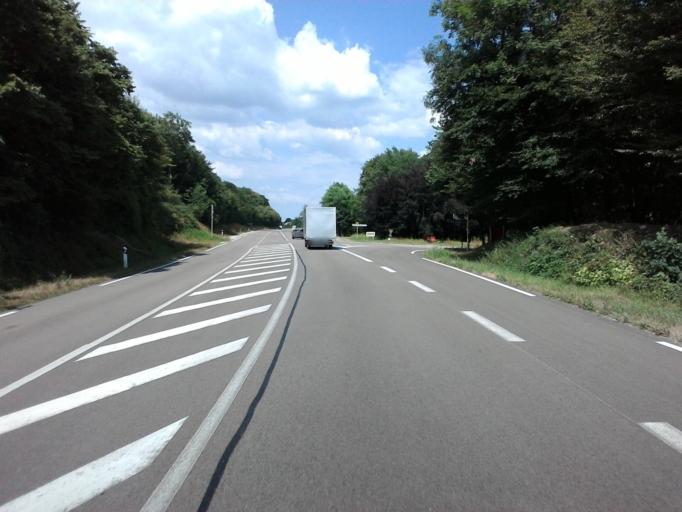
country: FR
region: Franche-Comte
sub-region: Departement du Doubs
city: Montferrand-le-Chateau
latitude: 47.1600
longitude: 5.9515
